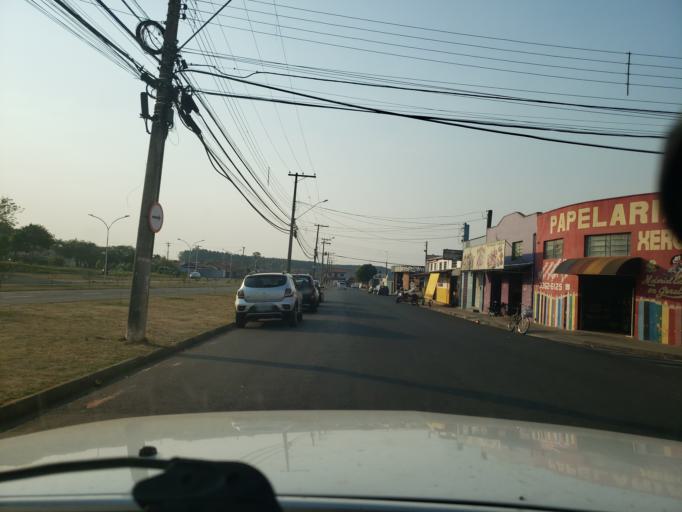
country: BR
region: Sao Paulo
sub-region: Moji-Guacu
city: Mogi-Gaucu
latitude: -22.3332
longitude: -46.9467
